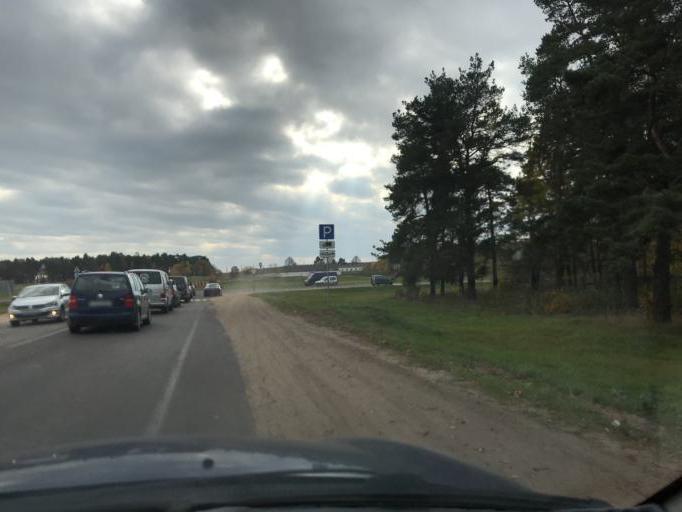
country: BY
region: Grodnenskaya
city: Lida
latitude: 53.8733
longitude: 25.2593
